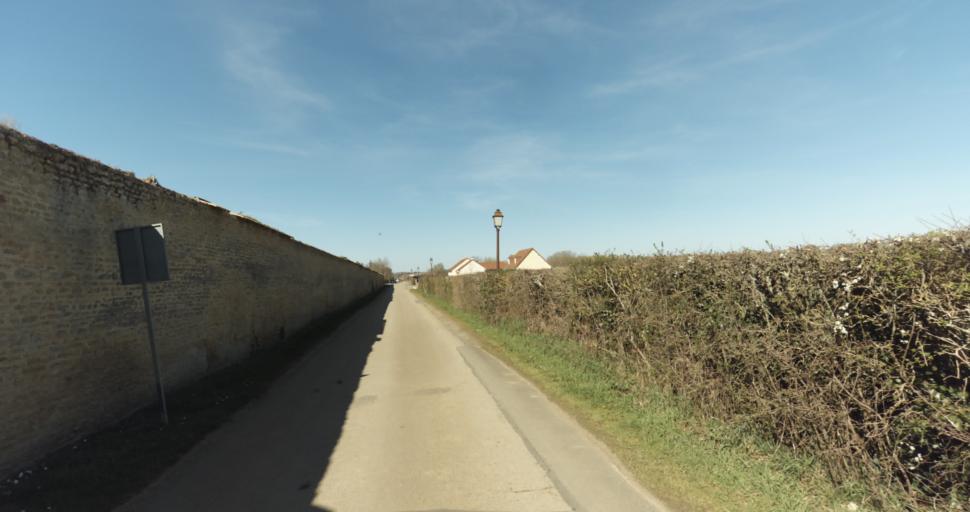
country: FR
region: Lower Normandy
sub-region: Departement du Calvados
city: Saint-Pierre-sur-Dives
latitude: 49.0409
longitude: -0.0262
